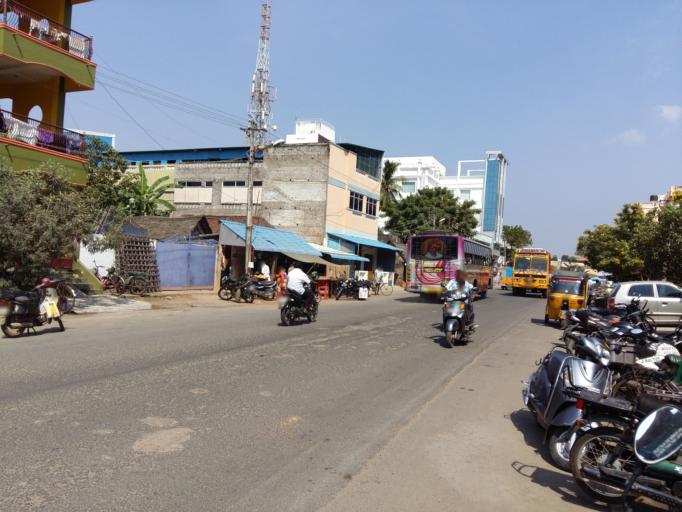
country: IN
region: Pondicherry
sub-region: Puducherry
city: Puducherry
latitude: 11.9138
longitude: 79.7544
